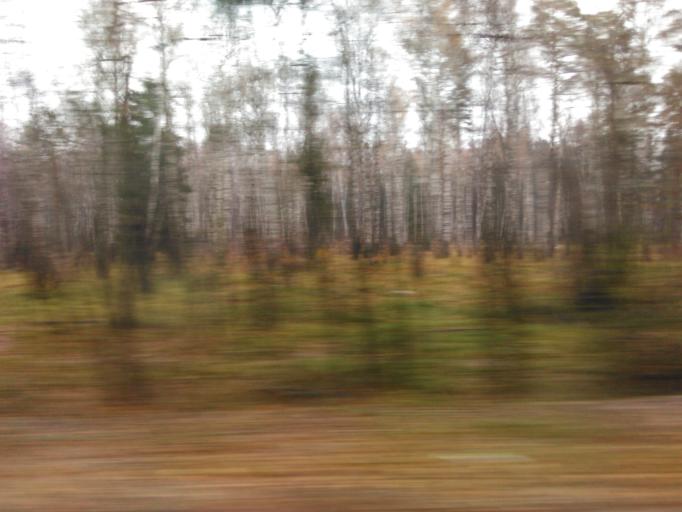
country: RU
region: Tatarstan
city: Osinovo
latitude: 55.8334
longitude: 48.8930
